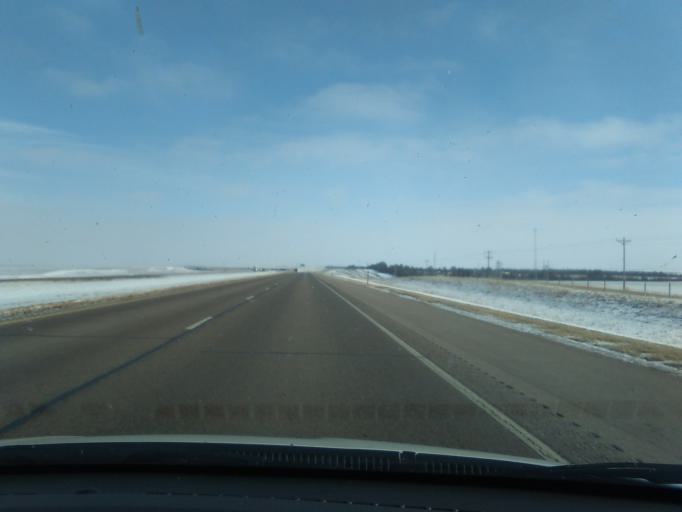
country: US
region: Nebraska
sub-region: Kimball County
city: Kimball
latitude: 41.1918
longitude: -103.7826
